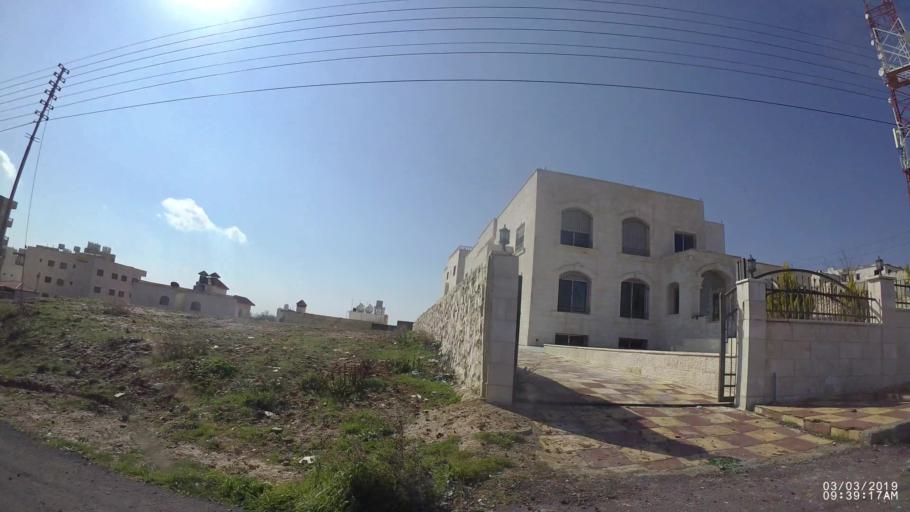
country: JO
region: Amman
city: Al Jubayhah
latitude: 31.9995
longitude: 35.8968
